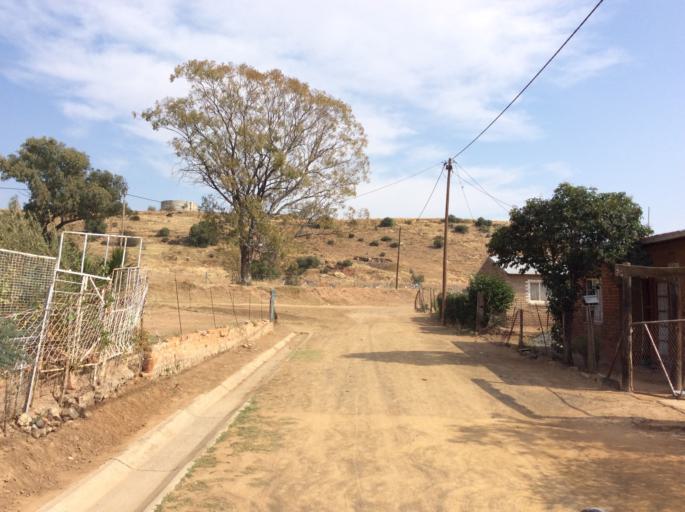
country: ZA
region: Orange Free State
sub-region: Xhariep District Municipality
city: Dewetsdorp
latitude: -29.5871
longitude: 26.6753
